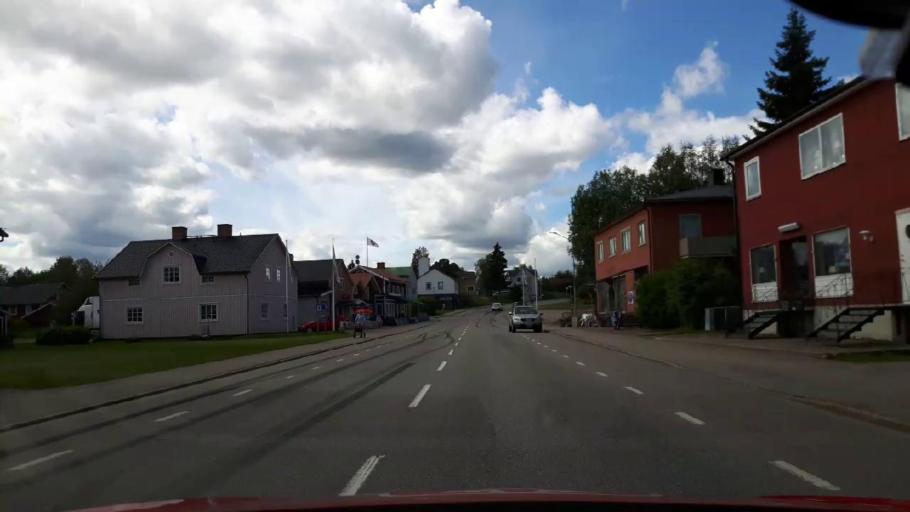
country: SE
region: Jaemtland
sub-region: Harjedalens Kommun
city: Sveg
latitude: 61.8514
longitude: 14.0767
